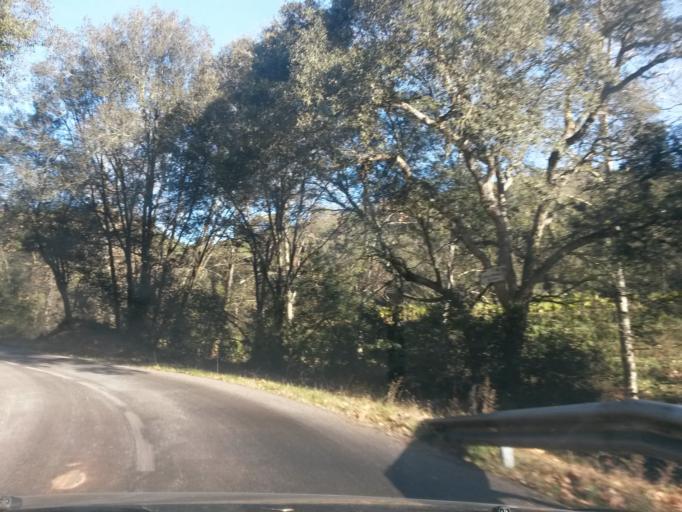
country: ES
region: Catalonia
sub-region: Provincia de Girona
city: Sant Gregori
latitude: 41.9897
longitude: 2.6814
